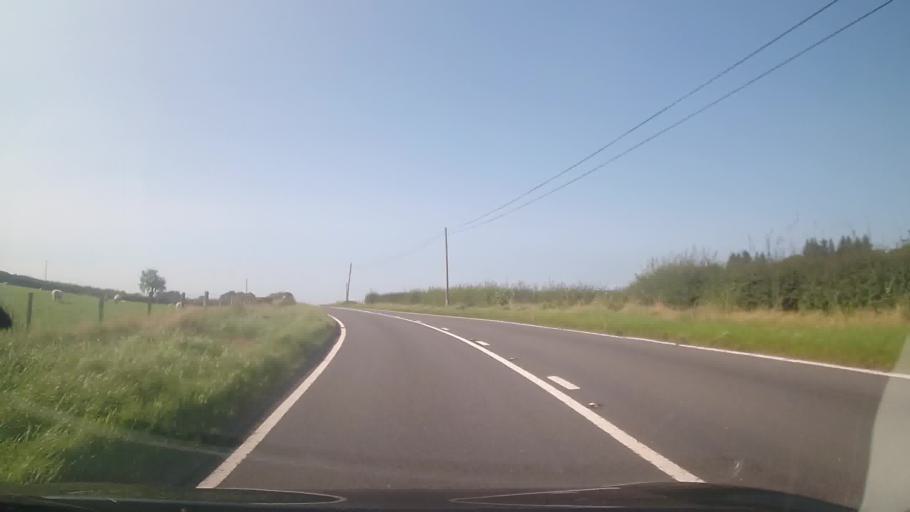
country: GB
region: Wales
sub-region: Sir Powys
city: Builth Wells
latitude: 52.1397
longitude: -3.5600
